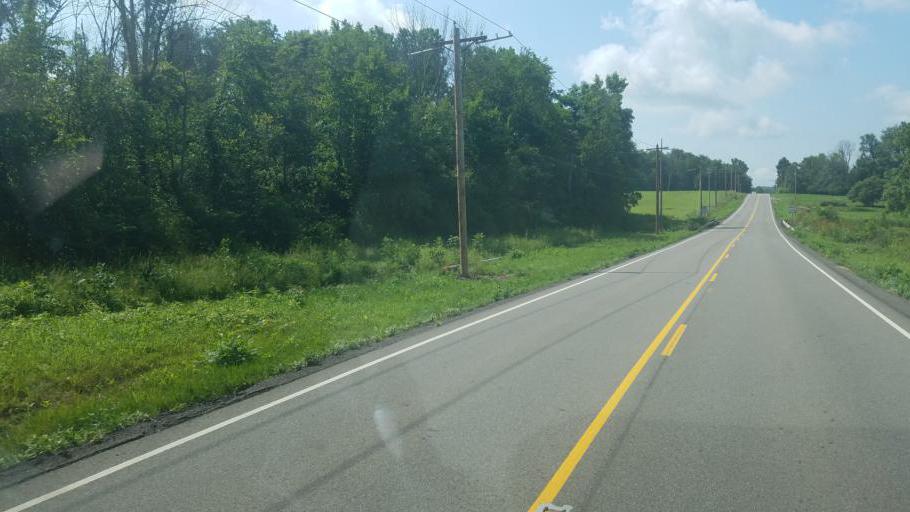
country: US
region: Ohio
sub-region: Licking County
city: Utica
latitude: 40.1882
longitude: -82.5178
